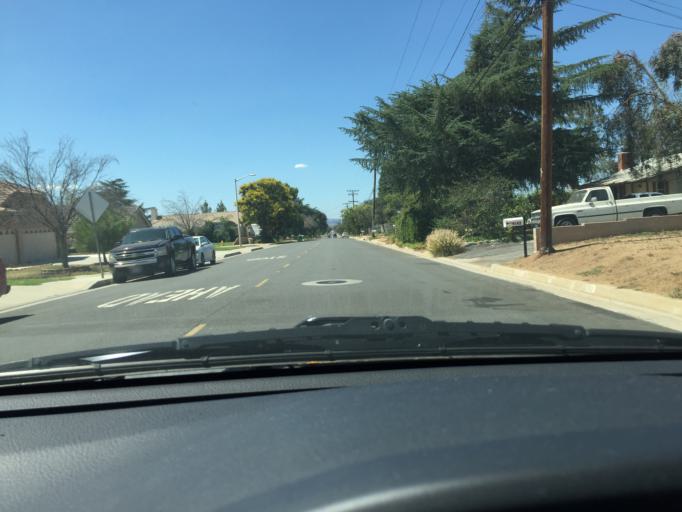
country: US
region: California
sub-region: Riverside County
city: Calimesa
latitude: 33.9995
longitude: -117.0397
